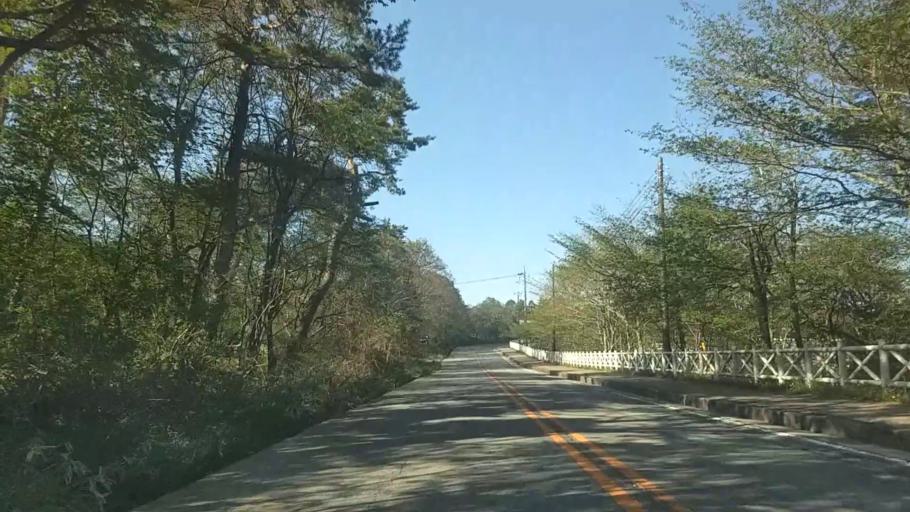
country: JP
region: Yamanashi
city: Nirasaki
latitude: 35.9281
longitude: 138.4076
